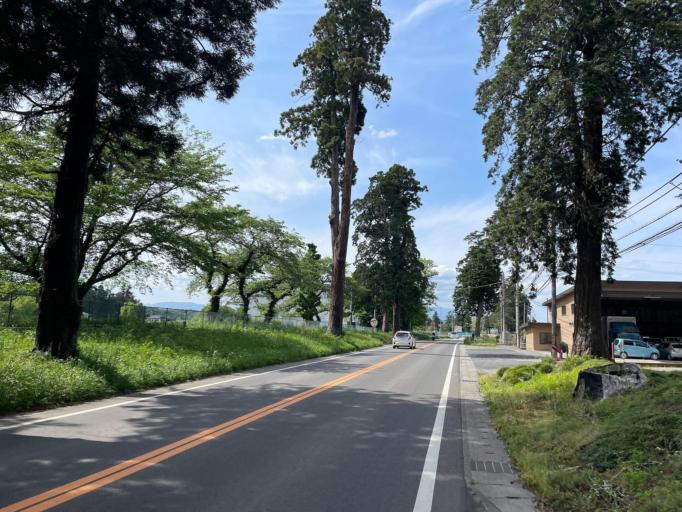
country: JP
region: Tochigi
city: Kanuma
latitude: 36.4891
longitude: 139.7586
